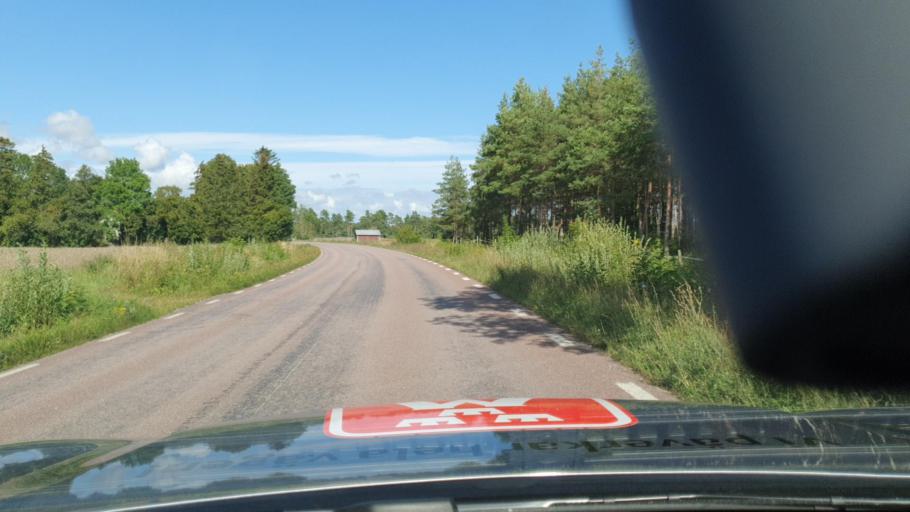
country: SE
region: Gotland
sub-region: Gotland
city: Hemse
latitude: 57.1373
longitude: 18.3473
